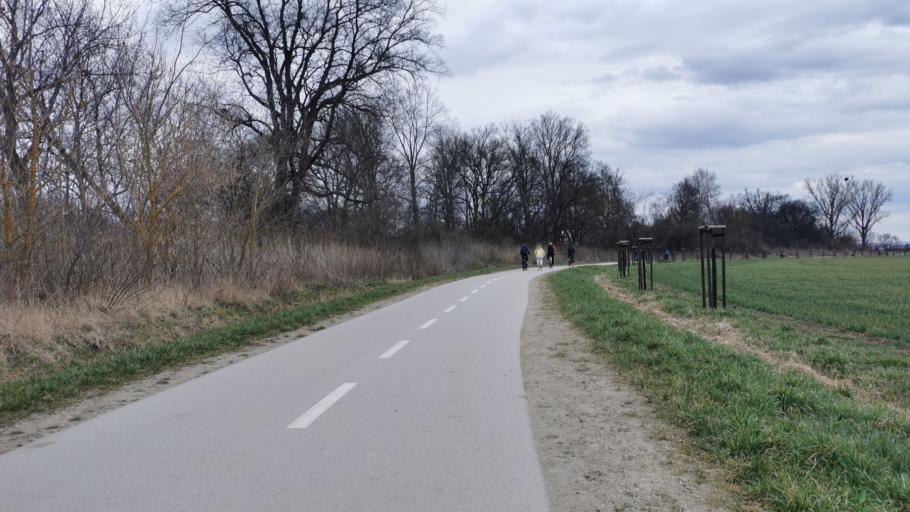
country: CZ
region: South Moravian
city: Luzice
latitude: 48.8001
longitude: 17.0998
